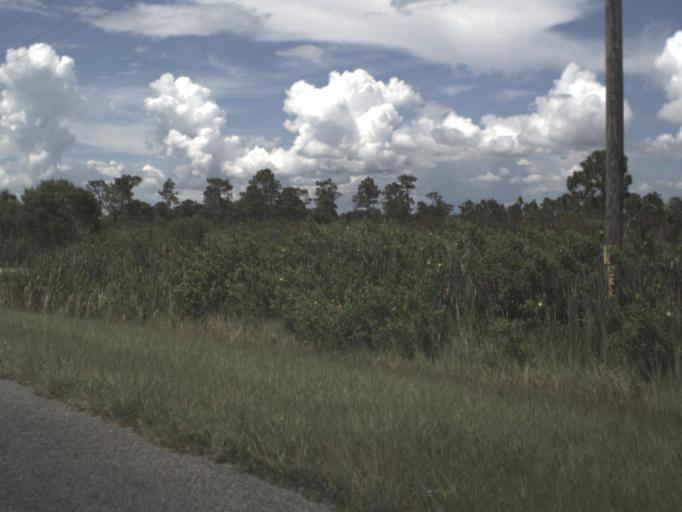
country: US
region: Florida
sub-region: Polk County
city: Babson Park
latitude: 27.8357
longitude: -81.3493
